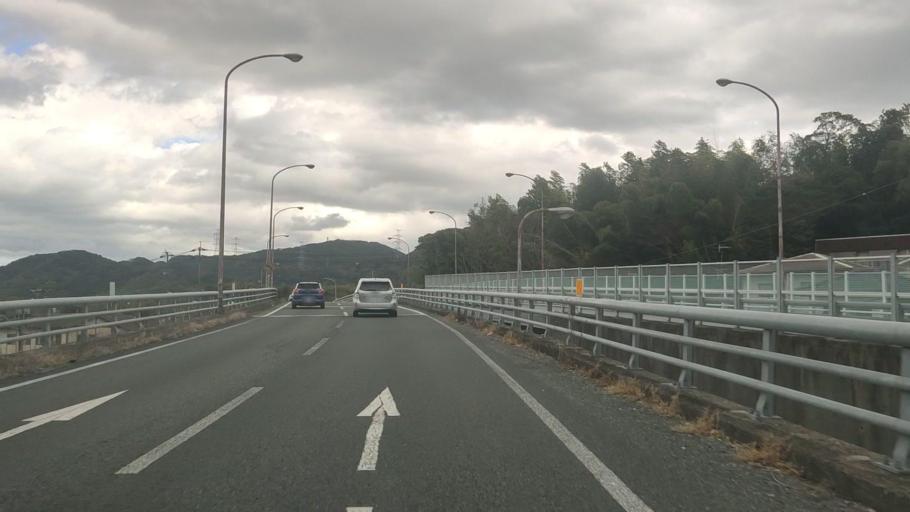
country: JP
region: Yamaguchi
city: Shimonoseki
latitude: 33.9736
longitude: 130.9465
